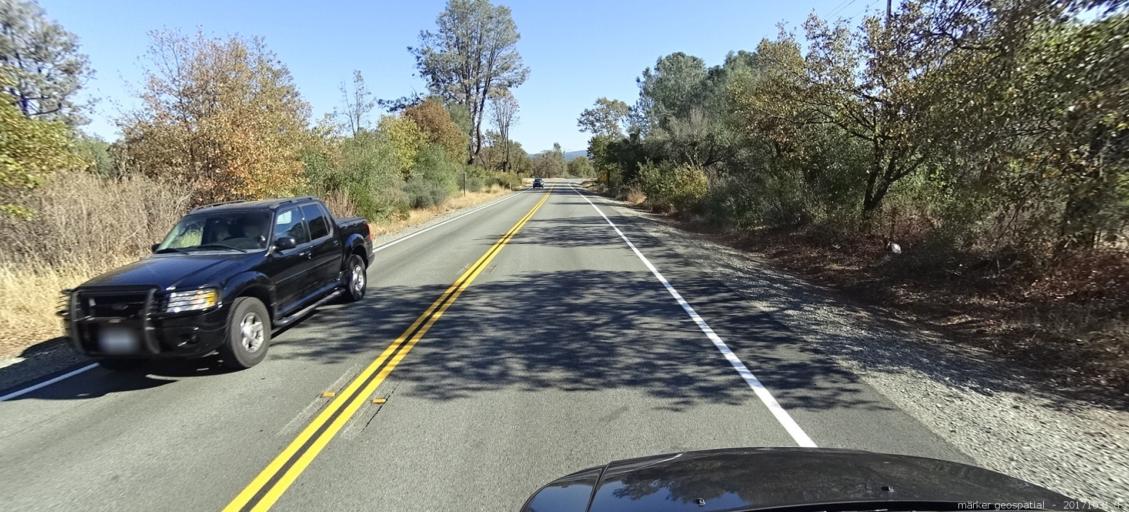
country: US
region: California
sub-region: Shasta County
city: Shingletown
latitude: 40.5138
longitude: -122.0273
